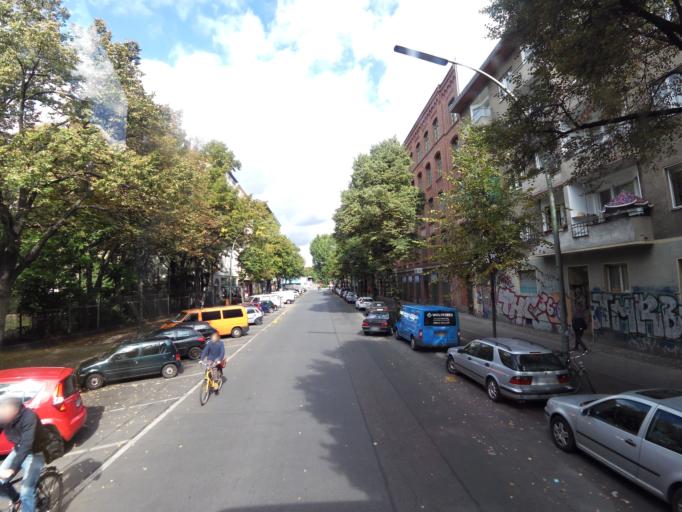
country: DE
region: Berlin
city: Berlin Treptow
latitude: 52.4962
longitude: 13.4309
